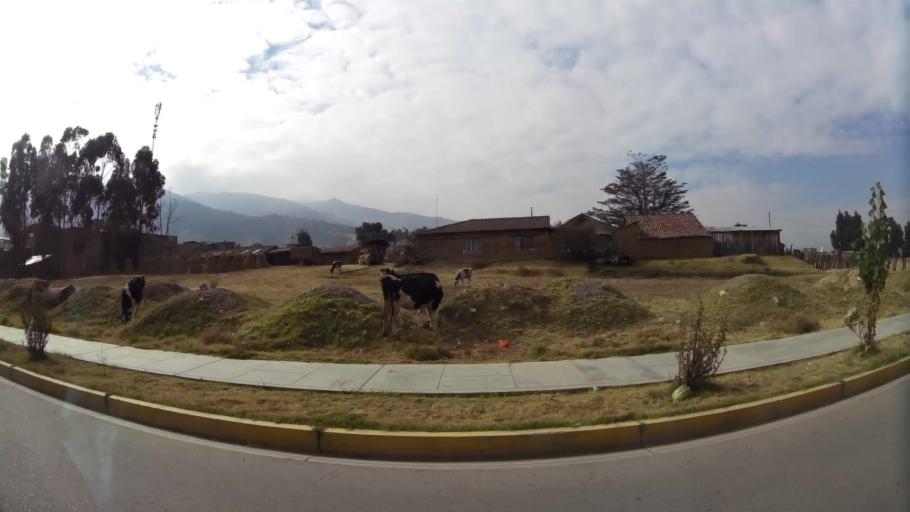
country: PE
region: Junin
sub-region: Provincia de Huancayo
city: Huancayo
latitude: -12.0559
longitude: -75.1996
